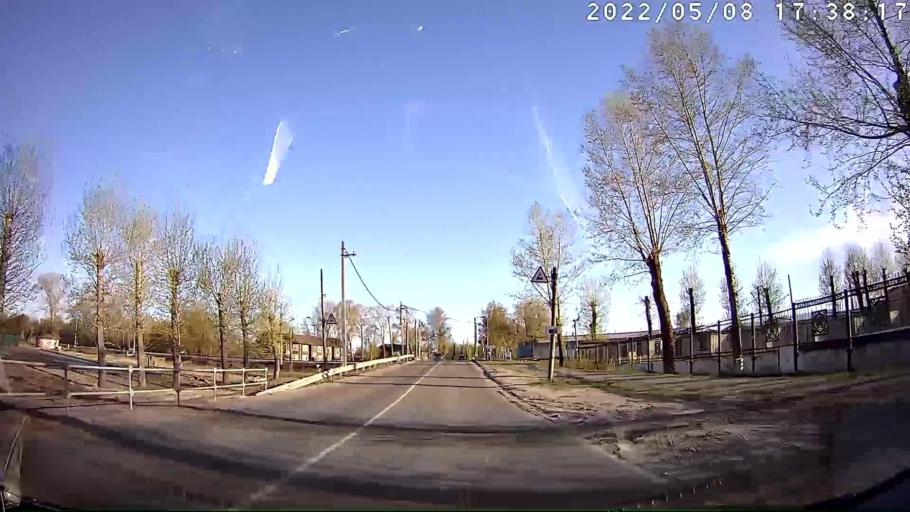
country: RU
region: Mariy-El
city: Volzhsk
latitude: 55.8611
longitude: 48.3718
